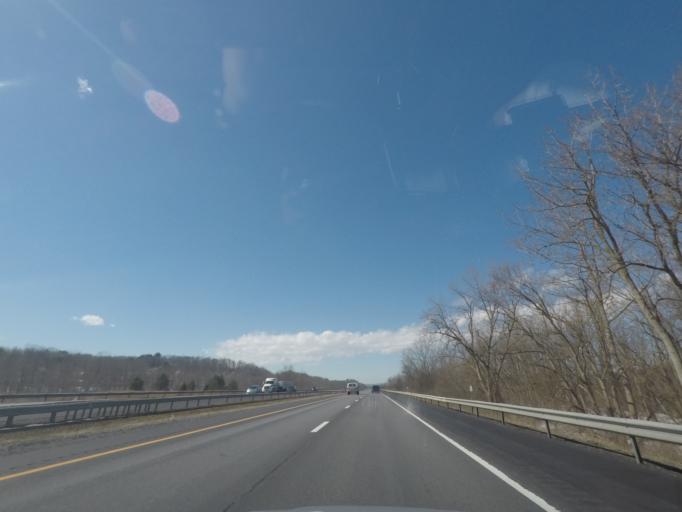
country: US
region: New York
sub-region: Montgomery County
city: Tribes Hill
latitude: 42.9341
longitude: -74.3210
